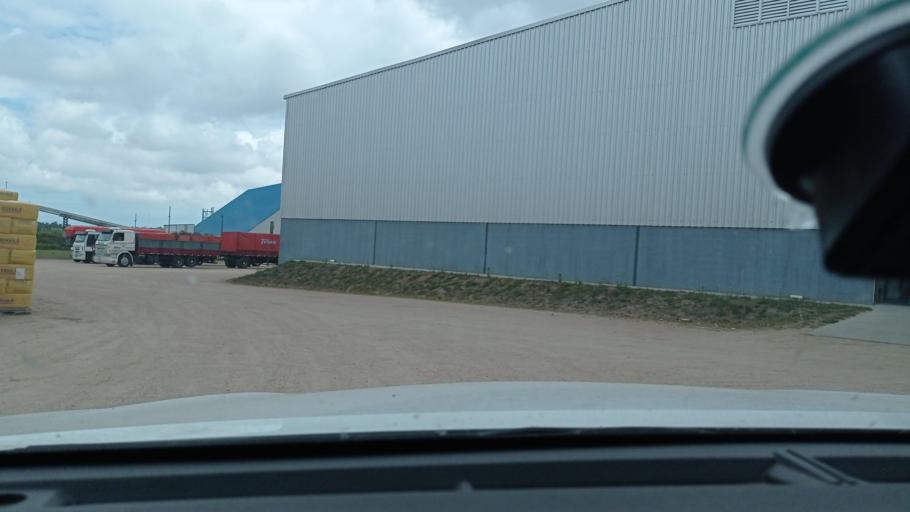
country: UY
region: Canelones
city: La Paz
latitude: -34.8189
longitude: -56.1933
